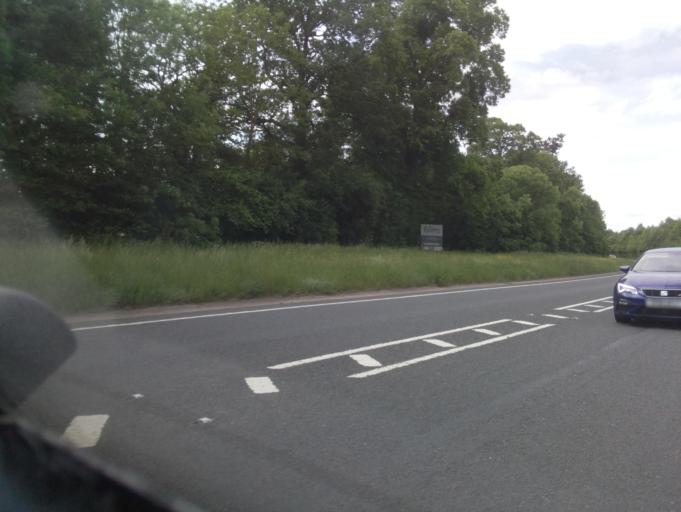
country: GB
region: England
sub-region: Worcestershire
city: Worcester
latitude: 52.1746
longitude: -2.2492
